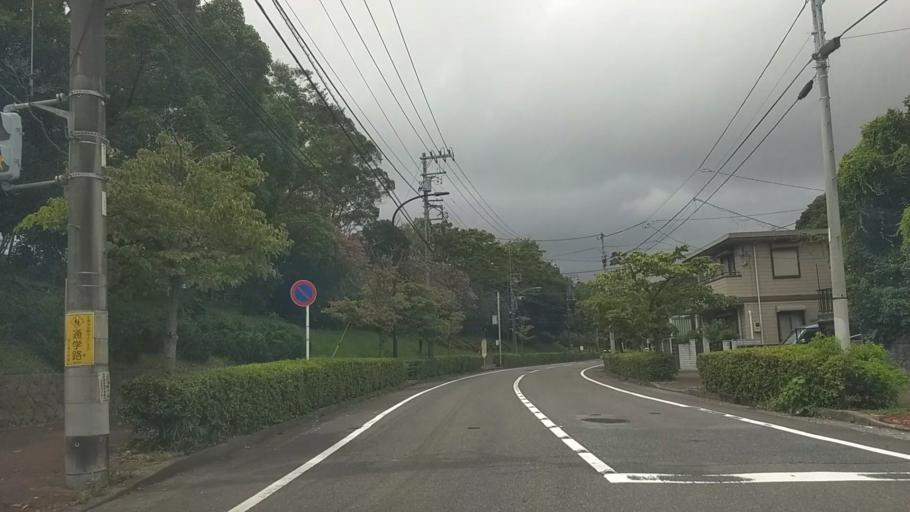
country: JP
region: Kanagawa
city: Yokosuka
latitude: 35.2688
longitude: 139.6668
